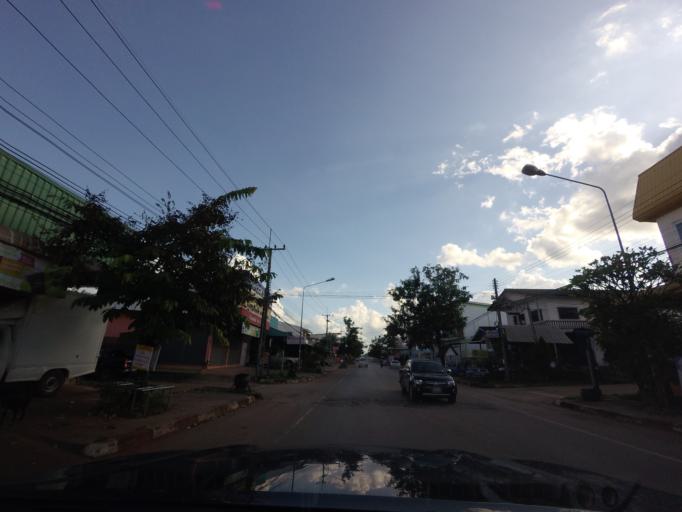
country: TH
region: Changwat Udon Thani
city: Ban Dung
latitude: 17.6957
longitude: 103.2587
